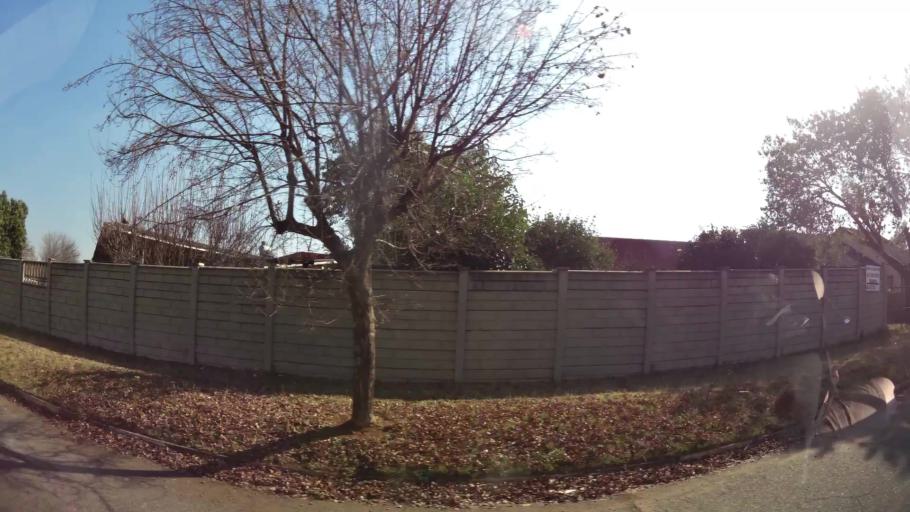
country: ZA
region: Gauteng
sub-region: West Rand District Municipality
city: Randfontein
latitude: -26.1666
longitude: 27.6997
